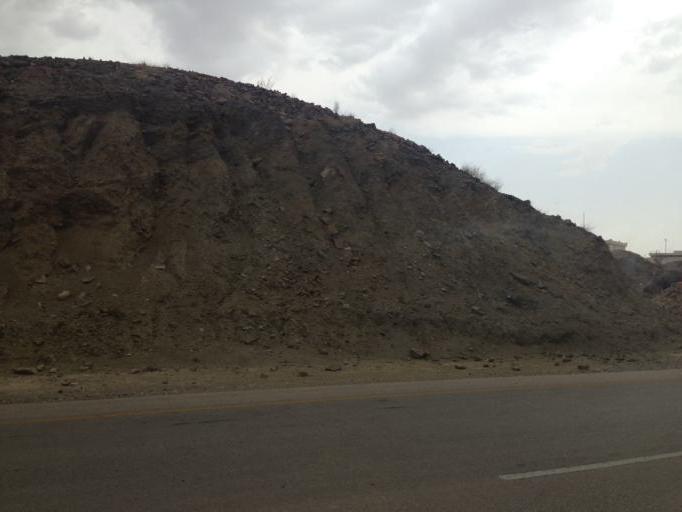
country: OM
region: Ash Sharqiyah
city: Badiyah
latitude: 22.5666
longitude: 59.0470
